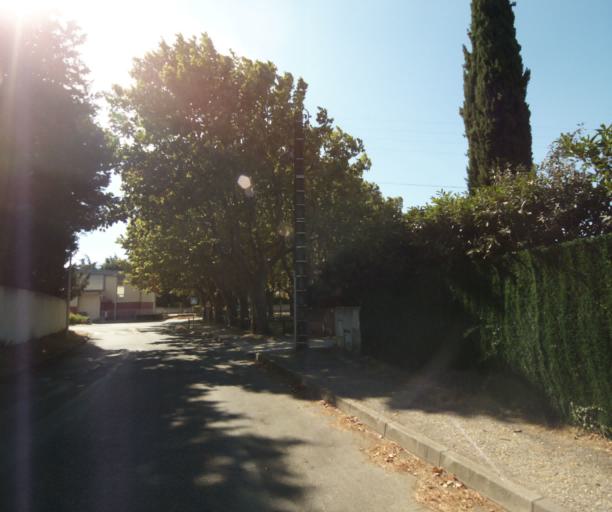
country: FR
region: Languedoc-Roussillon
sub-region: Departement du Gard
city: Bouillargues
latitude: 43.7990
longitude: 4.4368
